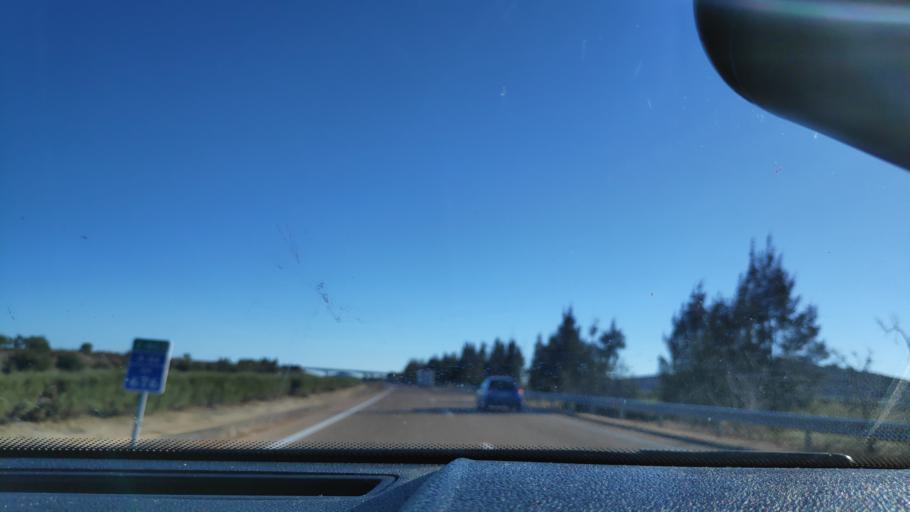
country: ES
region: Extremadura
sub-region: Provincia de Badajoz
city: Los Santos de Maimona
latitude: 38.4667
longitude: -6.3593
